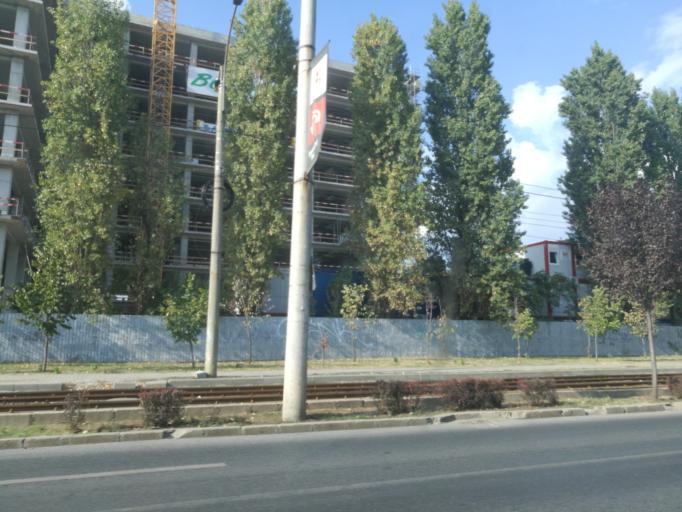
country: RO
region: Ilfov
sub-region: Comuna Chiajna
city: Rosu
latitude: 44.4727
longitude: 26.0559
